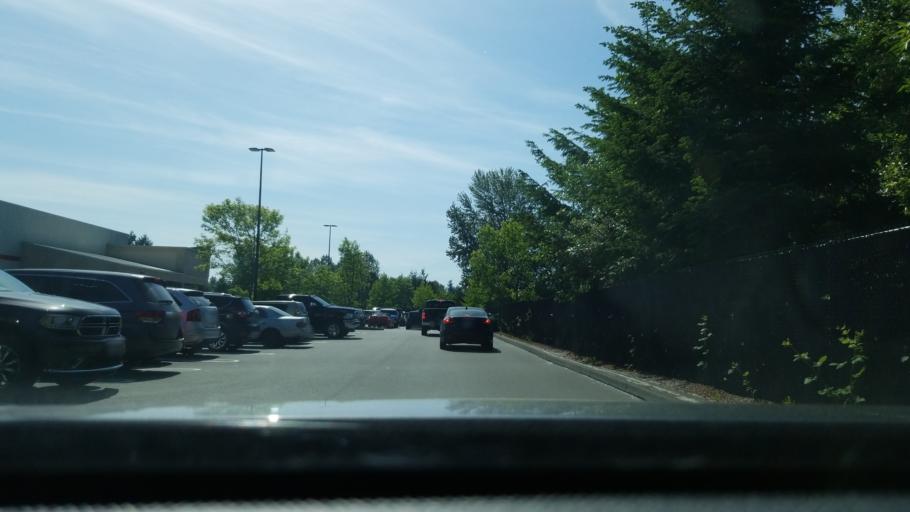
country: US
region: Washington
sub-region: Pierce County
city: Puyallup
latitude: 47.1565
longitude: -122.3074
